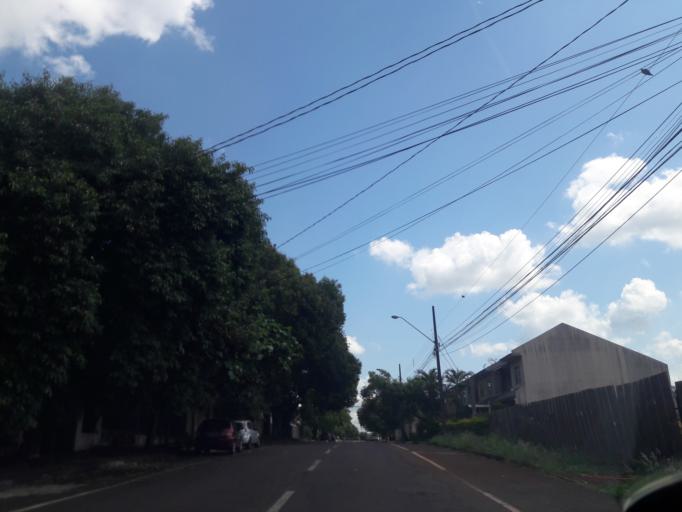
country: BR
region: Parana
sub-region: Cascavel
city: Cascavel
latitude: -24.9654
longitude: -53.4584
